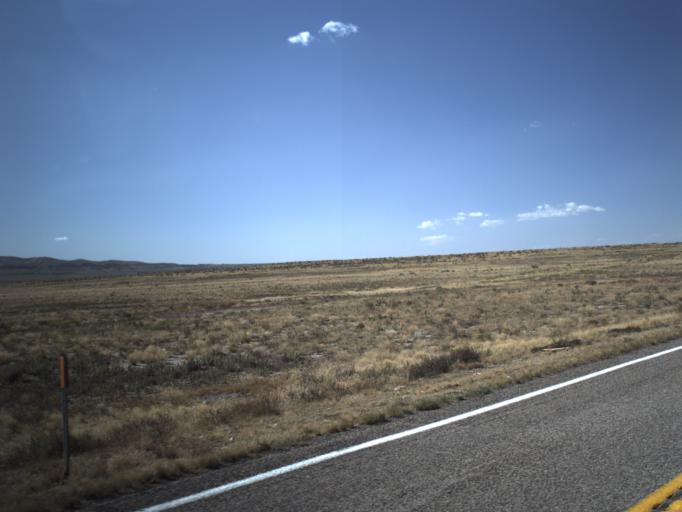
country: US
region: Utah
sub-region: Beaver County
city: Milford
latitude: 38.8123
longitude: -112.8686
